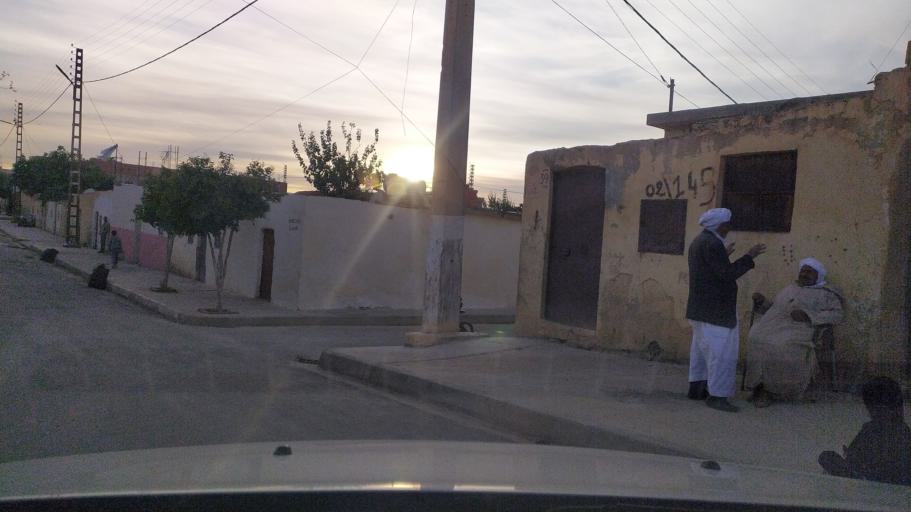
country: DZ
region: Tiaret
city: Frenda
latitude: 34.9010
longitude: 1.2362
